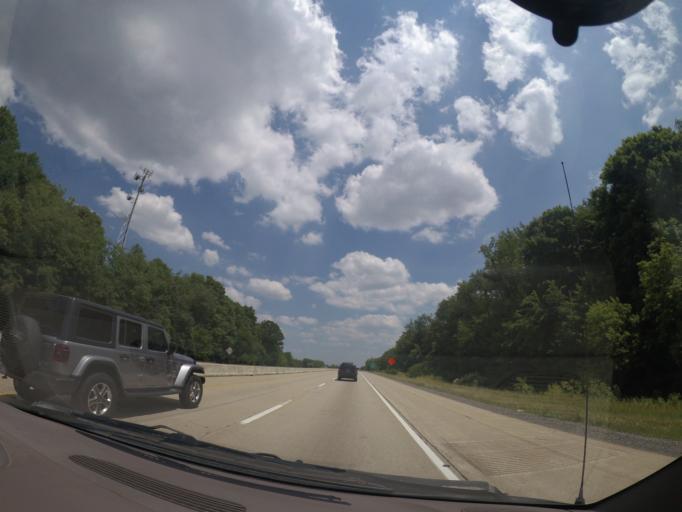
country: US
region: Indiana
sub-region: Saint Joseph County
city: Gulivoire Park
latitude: 41.6244
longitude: -86.1961
